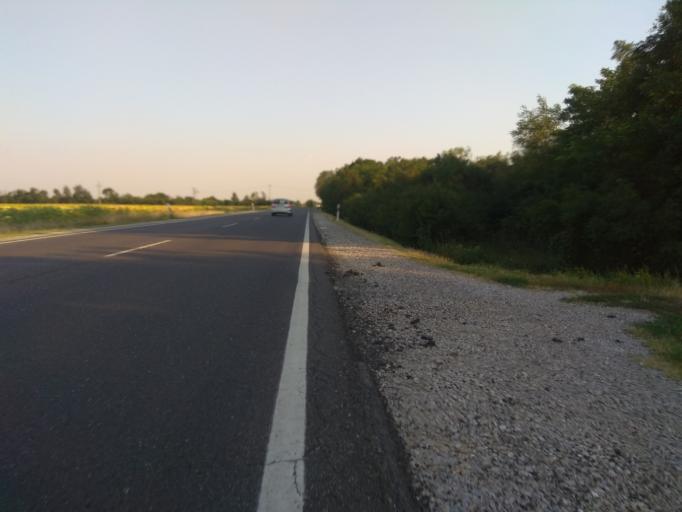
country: HU
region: Borsod-Abauj-Zemplen
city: Nyekladhaza
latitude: 47.9683
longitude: 20.8318
